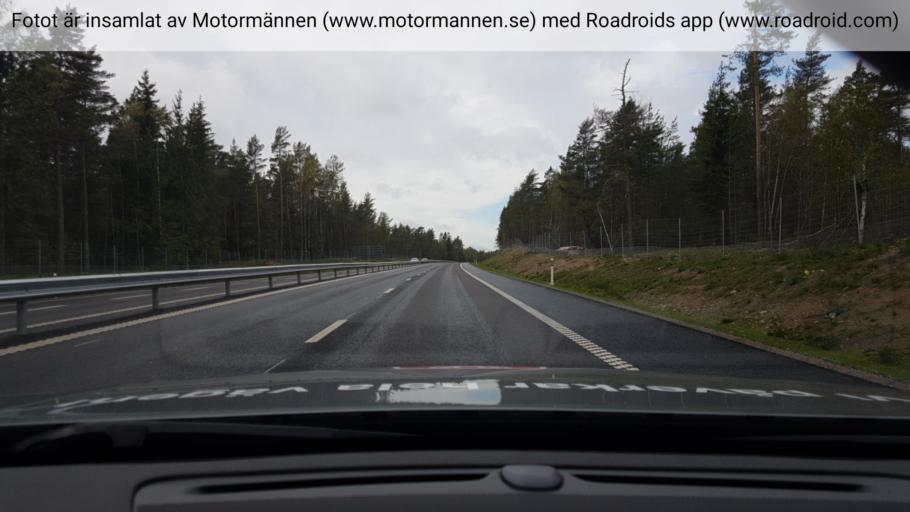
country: SE
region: Vaermland
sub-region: Hammaro Kommun
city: Skoghall
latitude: 59.3809
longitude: 13.3983
